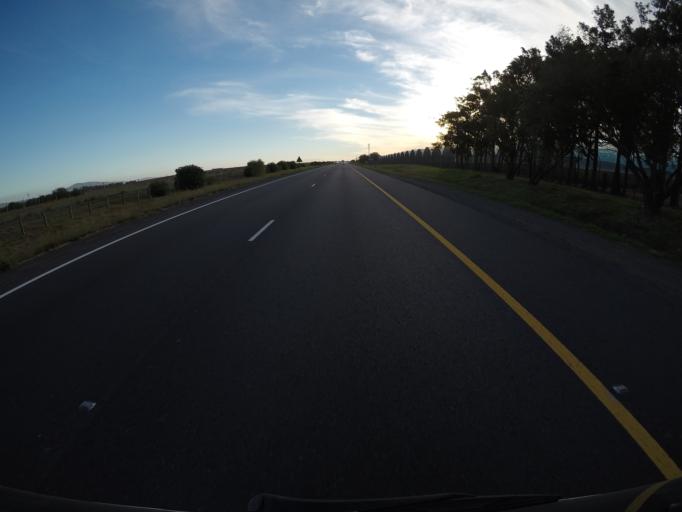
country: ZA
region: Western Cape
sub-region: City of Cape Town
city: Kraaifontein
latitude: -33.8093
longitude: 18.8289
